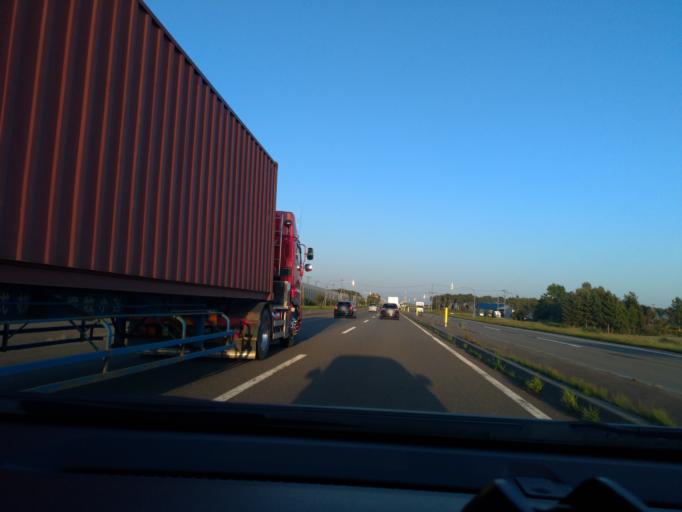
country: JP
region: Hokkaido
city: Tobetsu
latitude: 43.1802
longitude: 141.4746
